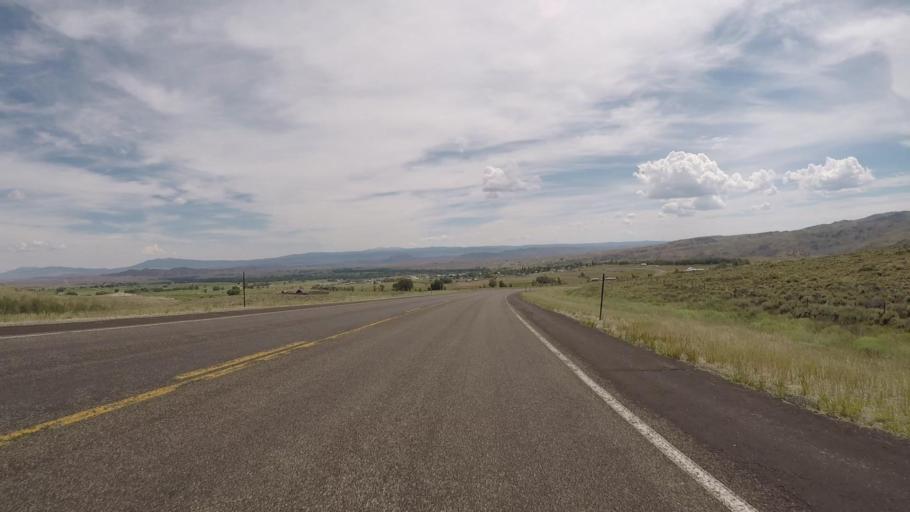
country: US
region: Wyoming
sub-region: Carbon County
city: Saratoga
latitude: 41.2053
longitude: -106.8160
